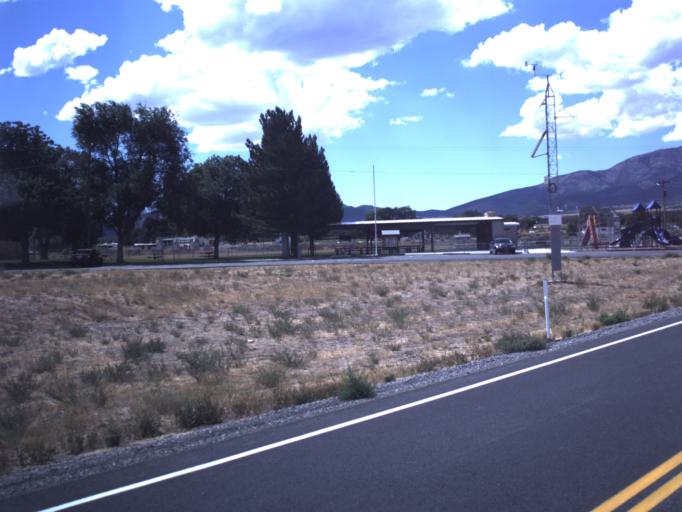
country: US
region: Utah
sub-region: Tooele County
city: Tooele
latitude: 40.3374
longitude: -112.4600
